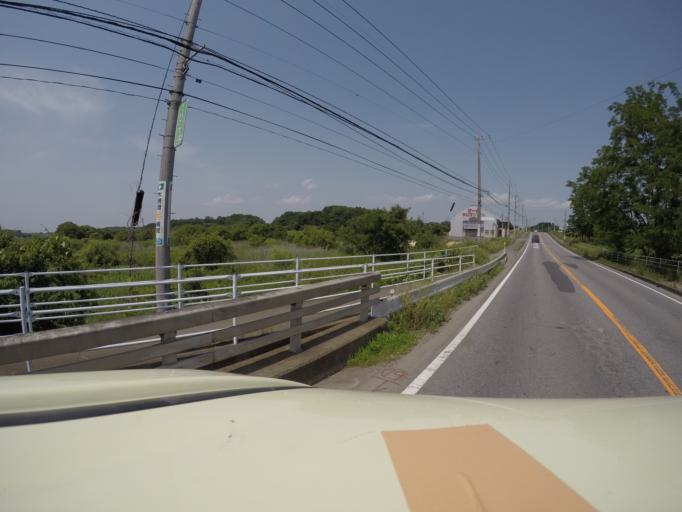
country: JP
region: Ibaraki
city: Iwai
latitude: 36.0339
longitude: 139.9087
